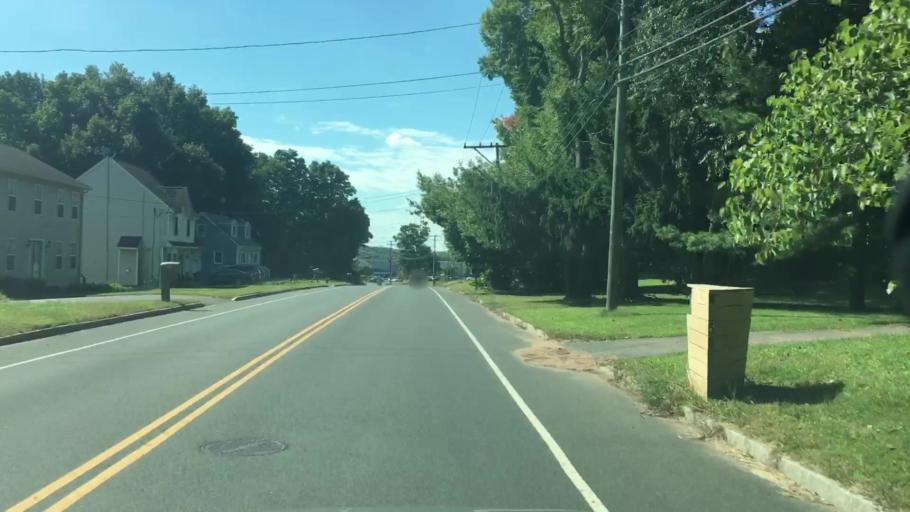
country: US
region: Connecticut
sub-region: Hartford County
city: Manchester
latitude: 41.7970
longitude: -72.5440
